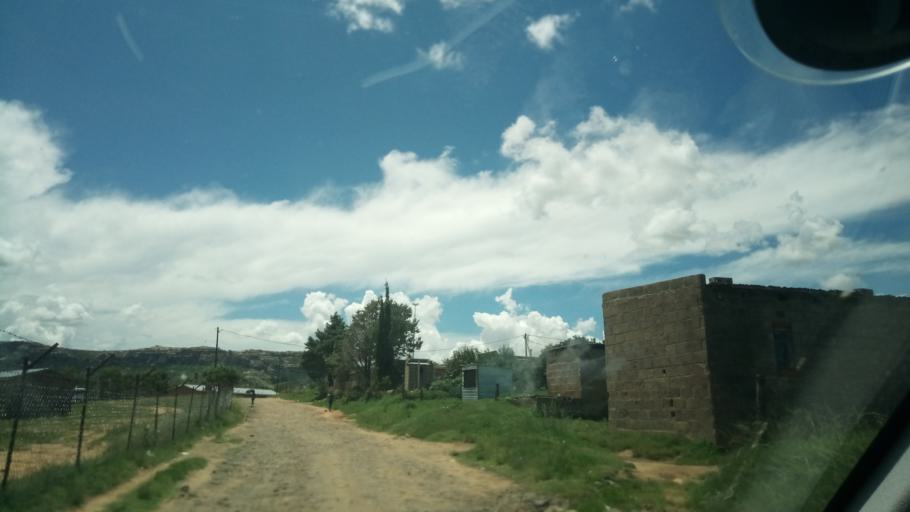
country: LS
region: Maseru
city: Maseru
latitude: -29.3644
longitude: 27.5419
